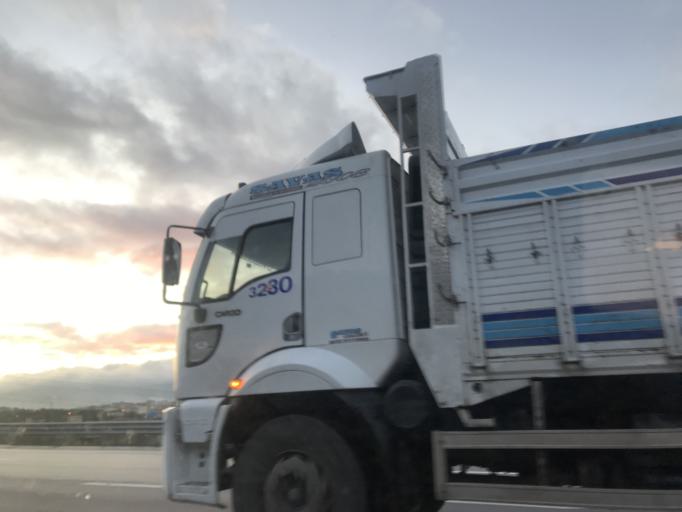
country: TR
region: Istanbul
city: Sultanbeyli
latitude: 40.9601
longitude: 29.3193
